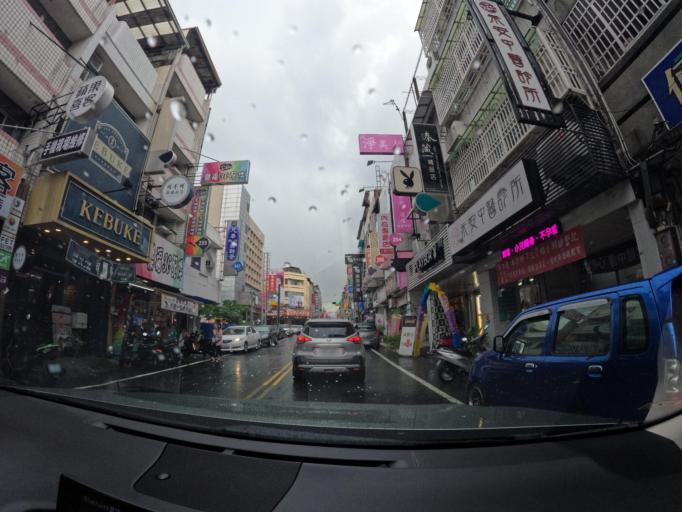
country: TW
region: Taiwan
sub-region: Nantou
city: Nantou
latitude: 23.9089
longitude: 120.6874
